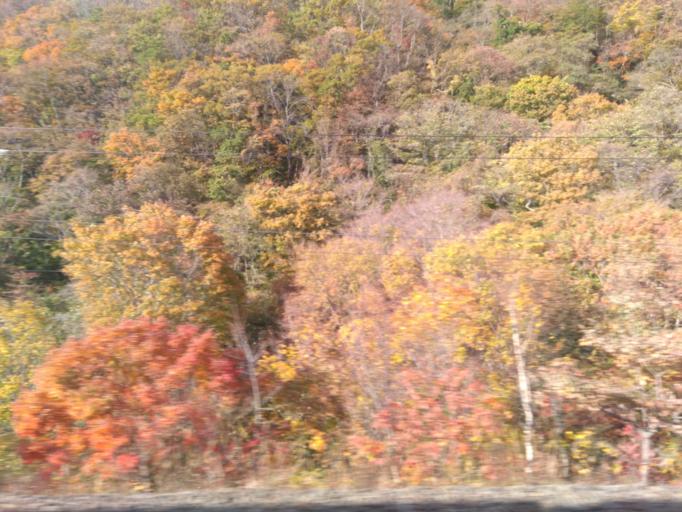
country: JP
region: Hokkaido
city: Niseko Town
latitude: 42.5909
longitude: 140.4710
